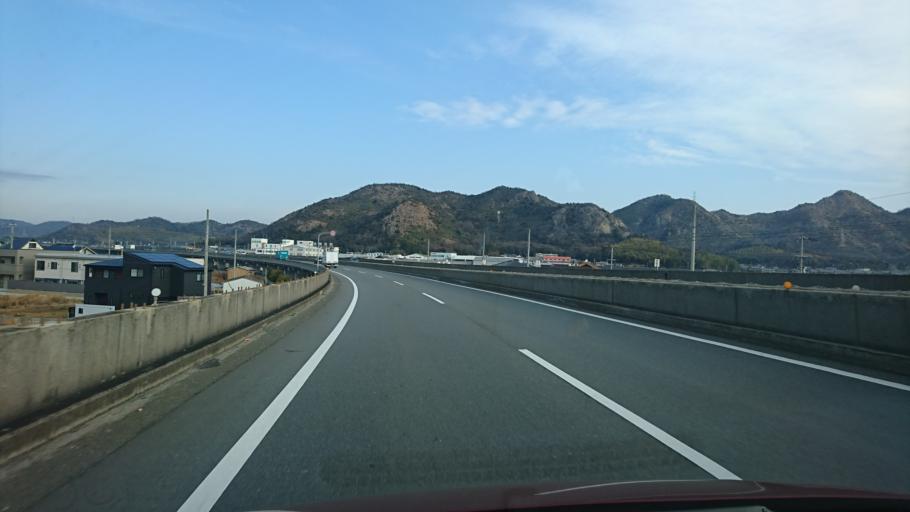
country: JP
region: Hyogo
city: Shirahamacho-usazakiminami
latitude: 34.8147
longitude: 134.7474
